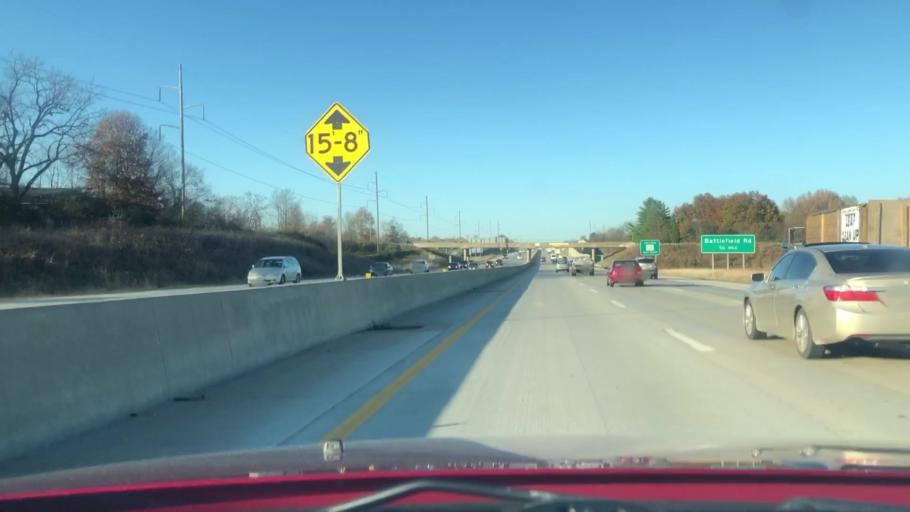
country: US
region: Missouri
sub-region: Greene County
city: Springfield
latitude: 37.1431
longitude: -93.2245
